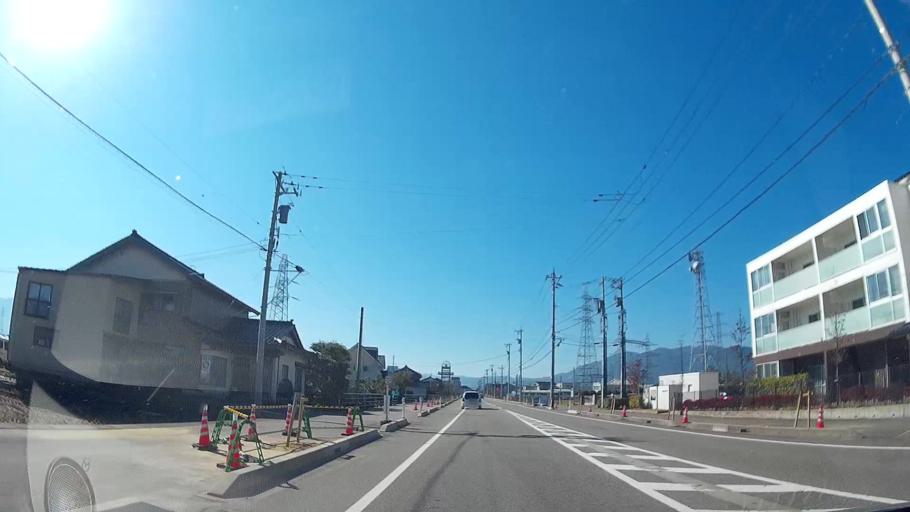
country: JP
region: Toyama
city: Fukumitsu
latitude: 36.5649
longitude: 136.8845
